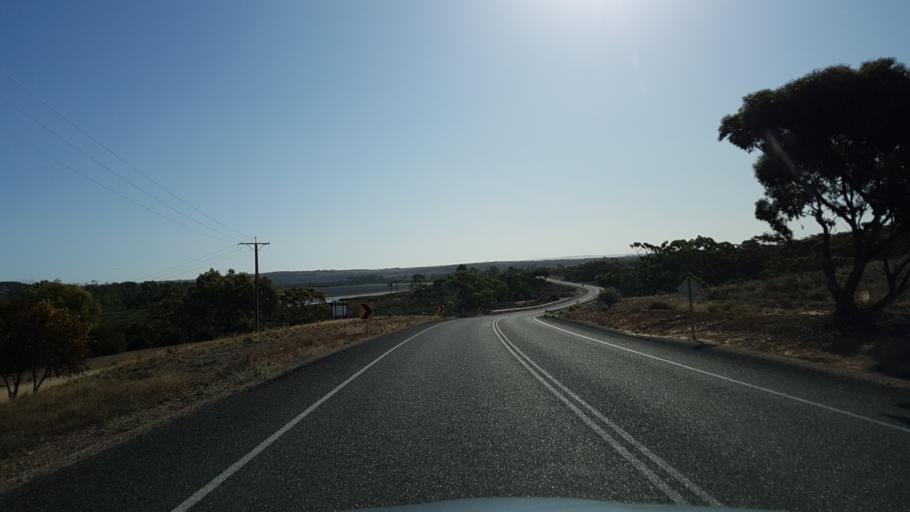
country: AU
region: South Australia
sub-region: Mid Murray
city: Mannum
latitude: -34.8563
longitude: 139.4184
